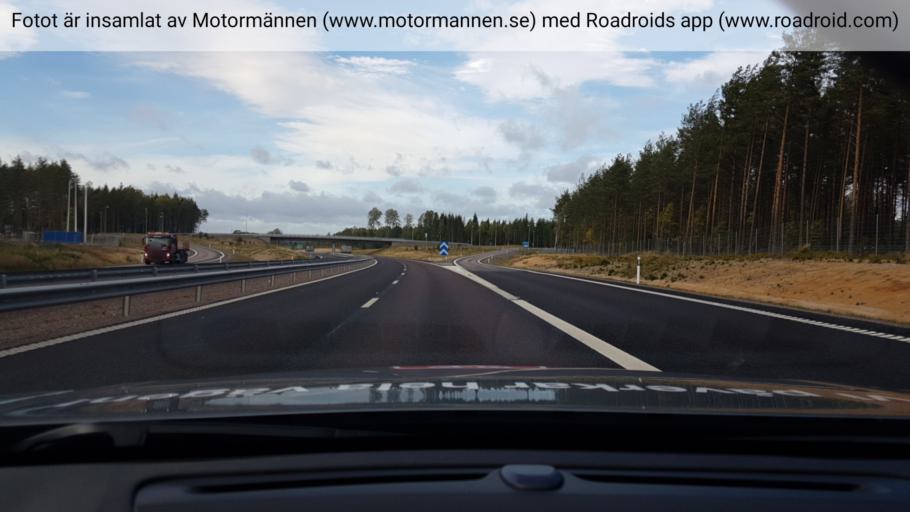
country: SE
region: Vaermland
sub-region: Kils Kommun
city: Kil
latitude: 59.3918
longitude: 13.2895
